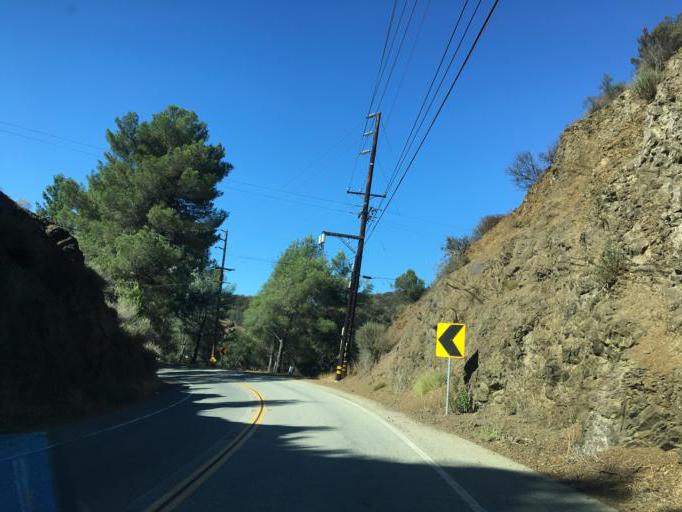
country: US
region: California
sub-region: Los Angeles County
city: Agoura
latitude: 34.0965
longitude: -118.6971
